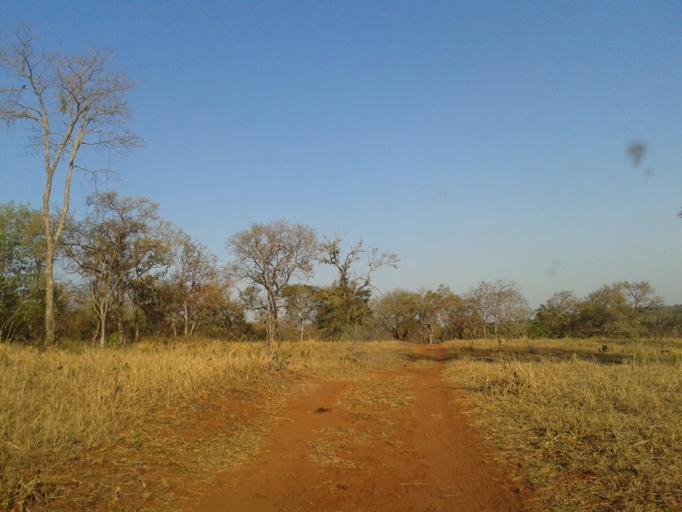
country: BR
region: Minas Gerais
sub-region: Campina Verde
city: Campina Verde
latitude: -19.2646
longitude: -49.6086
